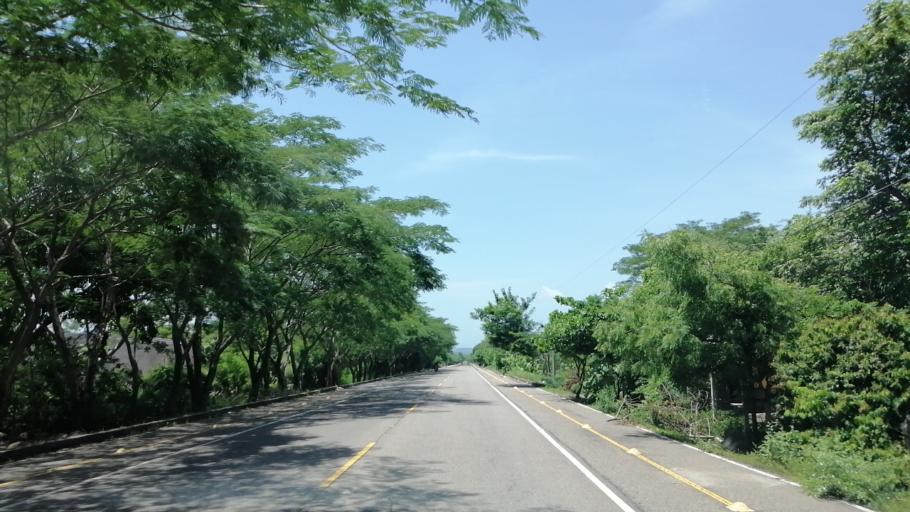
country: SV
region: Chalatenango
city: Nueva Concepcion
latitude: 14.1451
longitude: -89.3024
